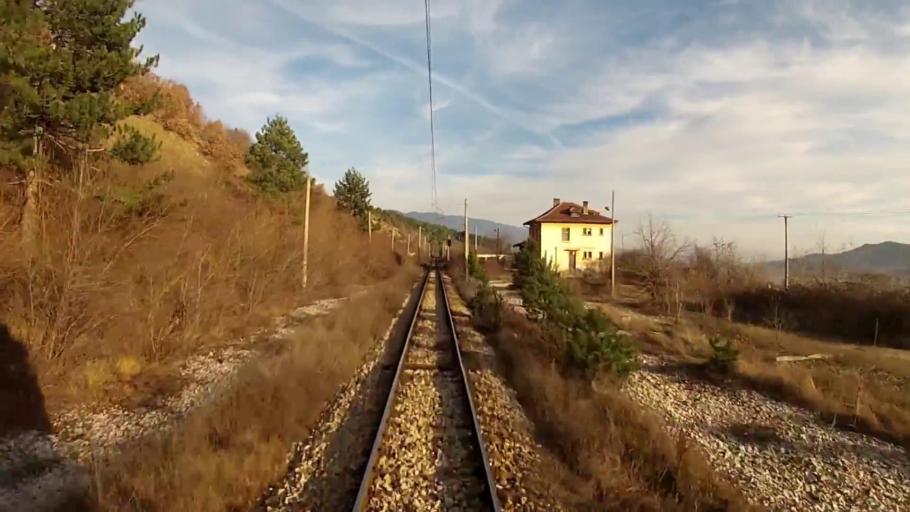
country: BG
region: Plovdiv
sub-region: Obshtina Karlovo
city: Klisura
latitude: 42.7225
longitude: 24.5935
